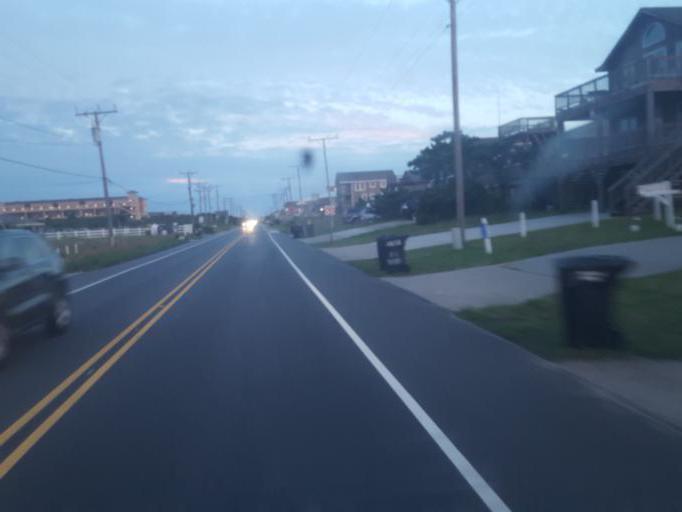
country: US
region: North Carolina
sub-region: Dare County
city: Kill Devil Hills
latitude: 36.0279
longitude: -75.6656
